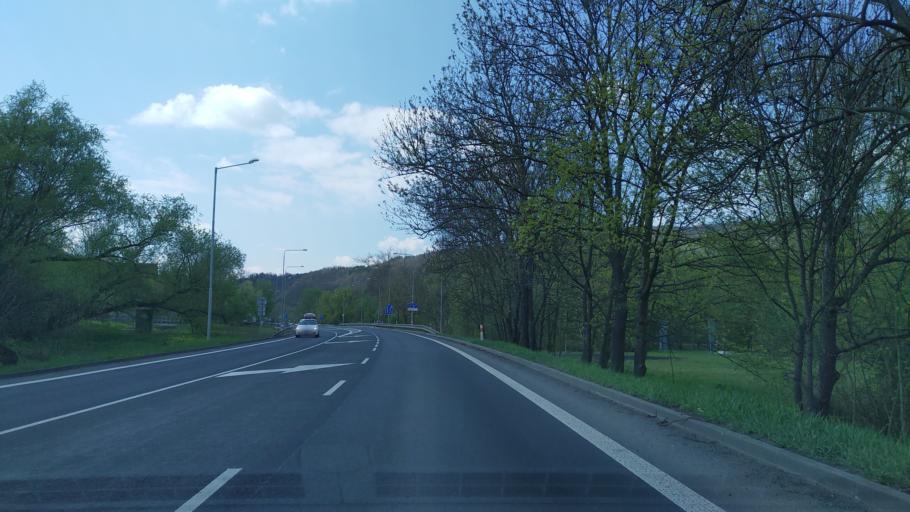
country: CZ
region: Ustecky
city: Bilina Kyselka
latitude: 50.5426
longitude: 13.7637
